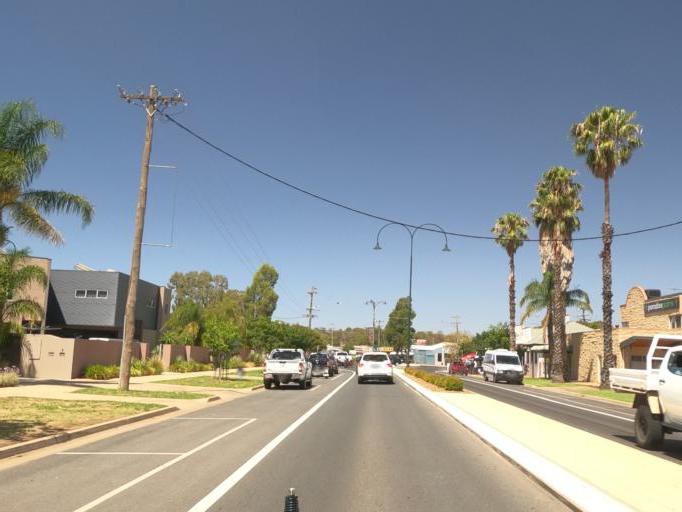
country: AU
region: New South Wales
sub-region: Corowa Shire
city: Mulwala
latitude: -35.9916
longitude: 146.0031
